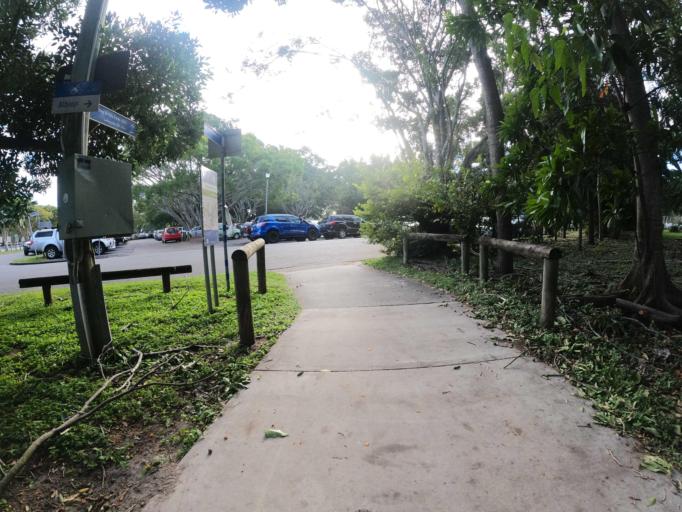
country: AU
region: Queensland
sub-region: Brisbane
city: Windsor
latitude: -27.4432
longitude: 153.0270
